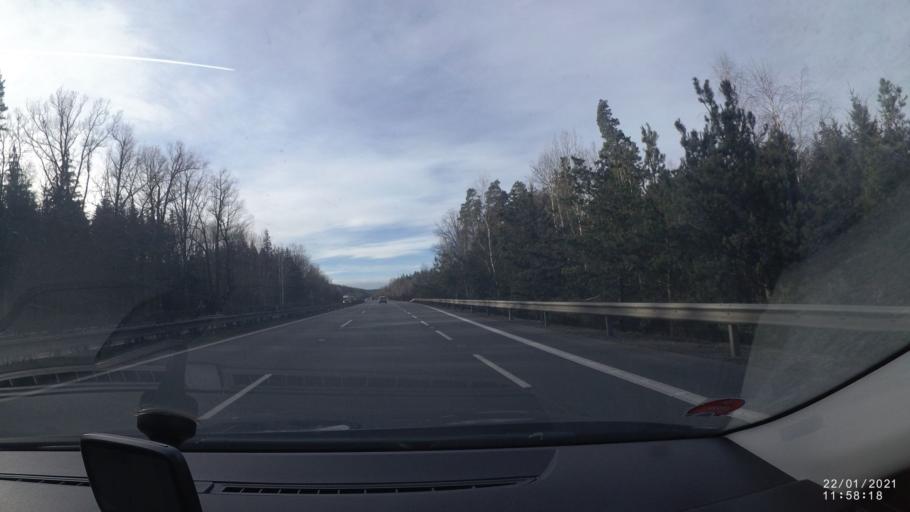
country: CZ
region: Plzensky
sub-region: Okres Rokycany
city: Rokycany
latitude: 49.7473
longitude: 13.5531
